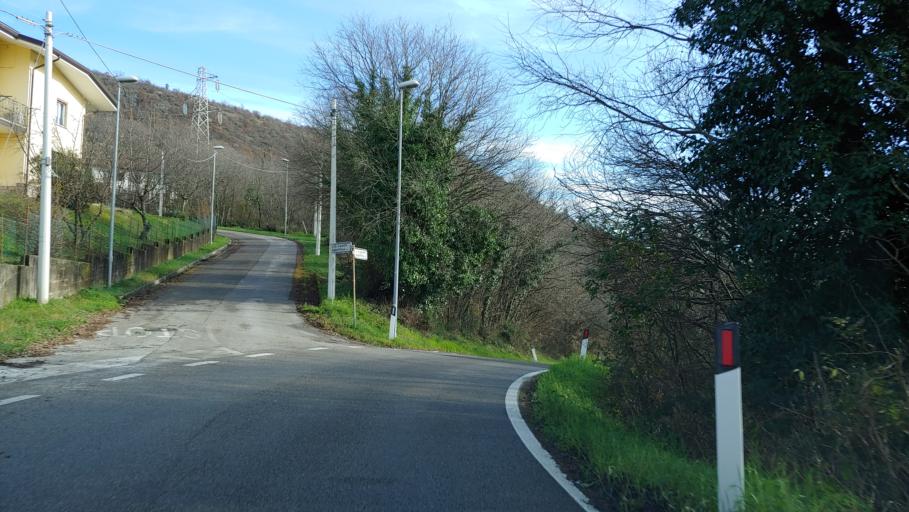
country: IT
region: Friuli Venezia Giulia
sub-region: Provincia di Gorizia
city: Monfalcone
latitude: 45.8197
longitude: 13.5840
